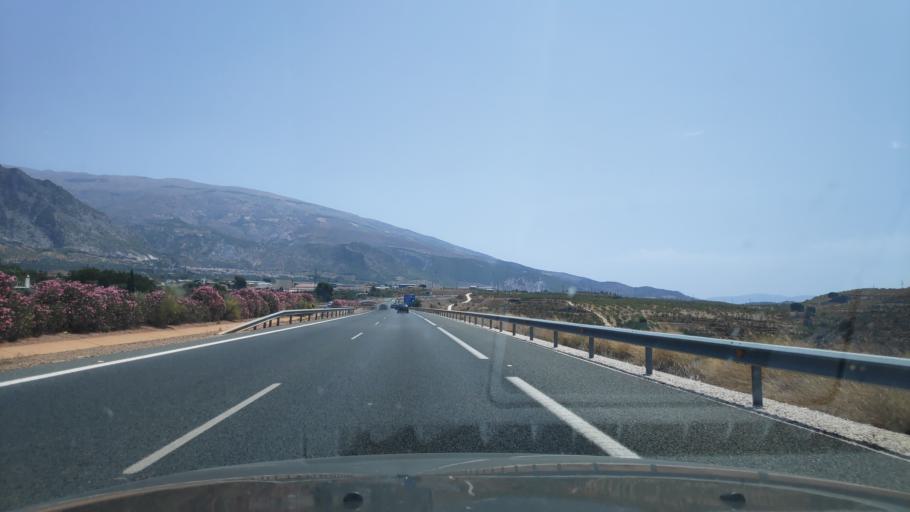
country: ES
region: Andalusia
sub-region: Provincia de Granada
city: Durcal
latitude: 36.9810
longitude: -3.5745
